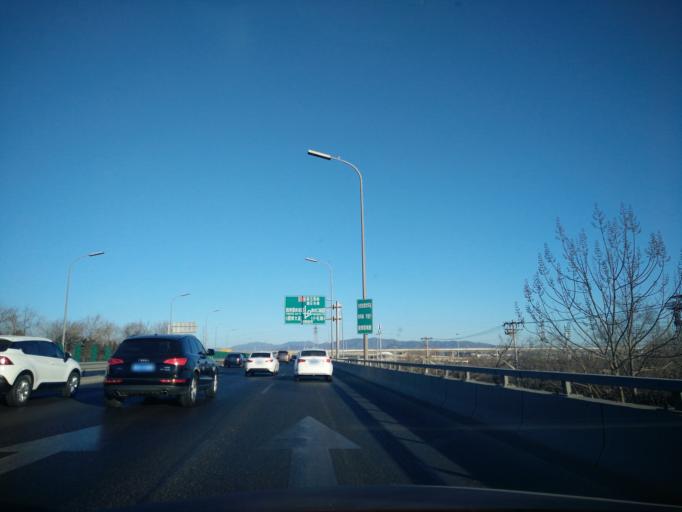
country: CN
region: Beijing
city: Lugu
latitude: 39.8588
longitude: 116.2124
